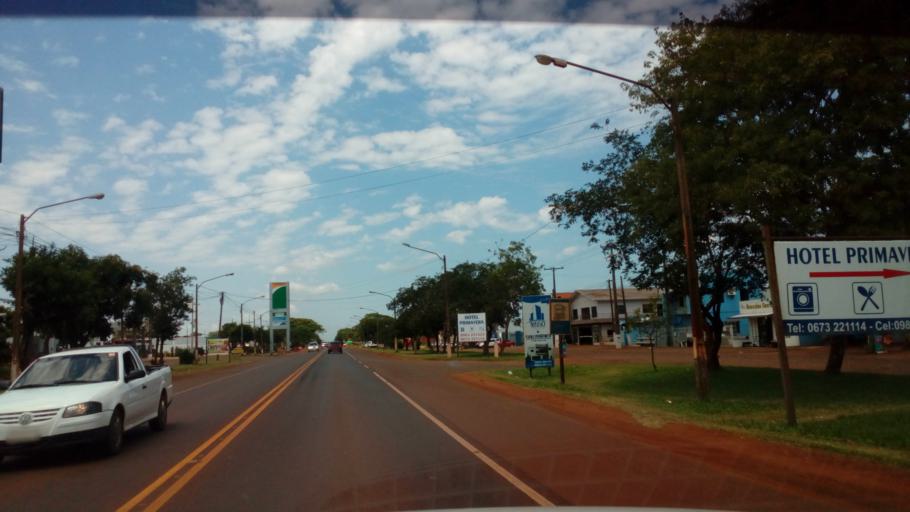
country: PY
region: Alto Parana
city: Santa Rita
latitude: -25.7788
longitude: -55.0763
